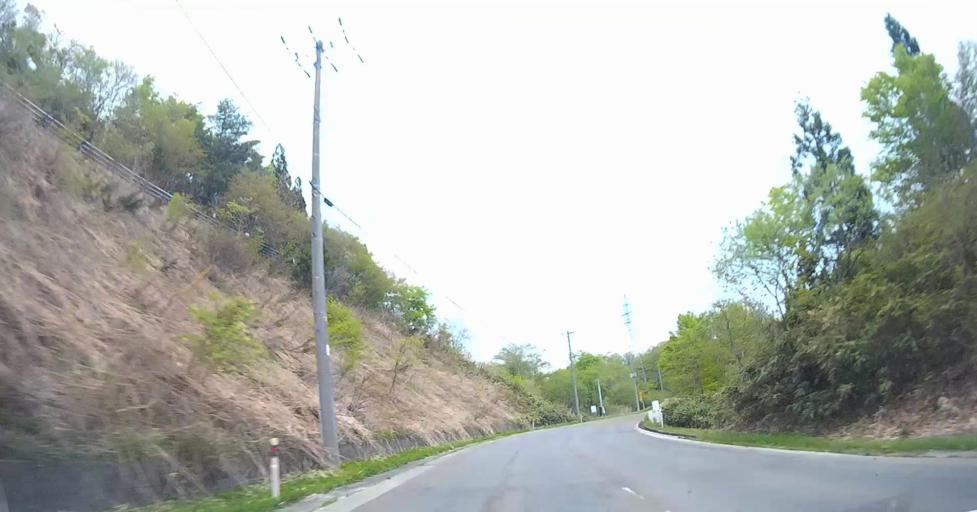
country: JP
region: Aomori
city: Goshogawara
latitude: 41.1084
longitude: 140.5373
